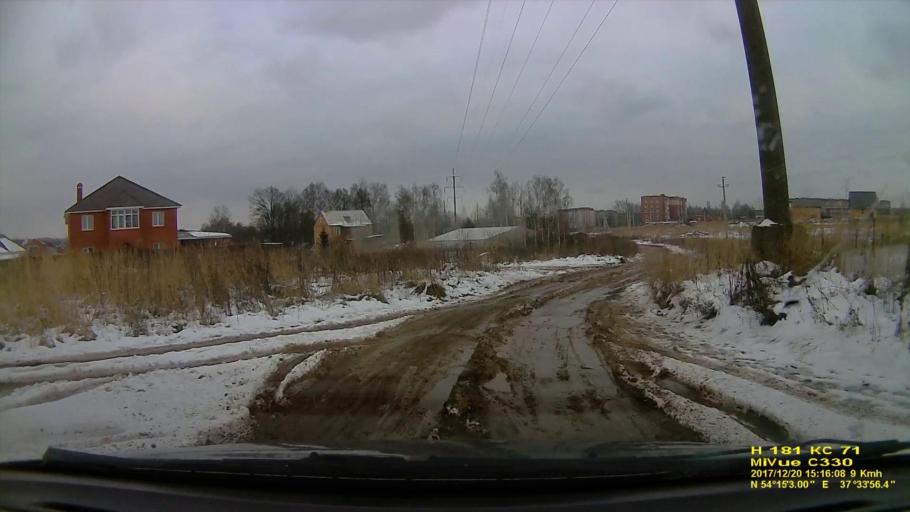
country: RU
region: Tula
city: Gorelki
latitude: 54.2508
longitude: 37.5657
